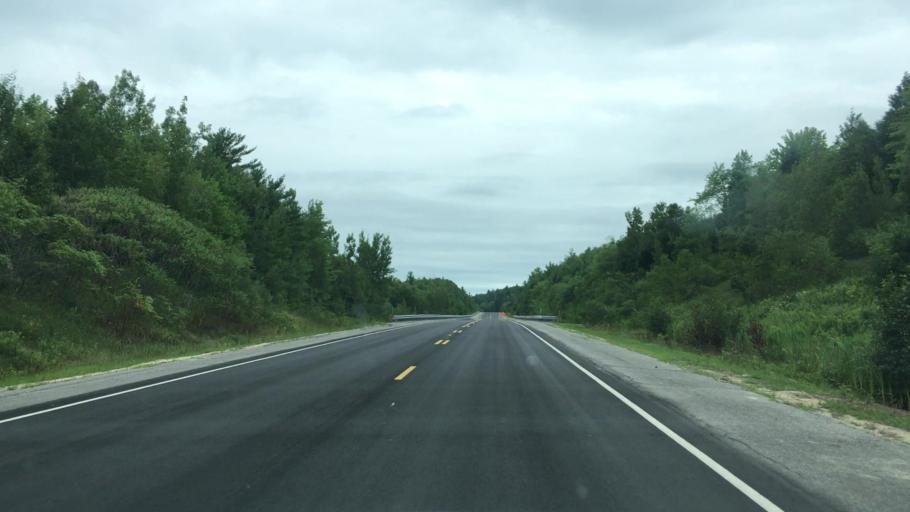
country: US
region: Maine
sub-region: Washington County
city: Cherryfield
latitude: 44.8882
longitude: -67.8566
